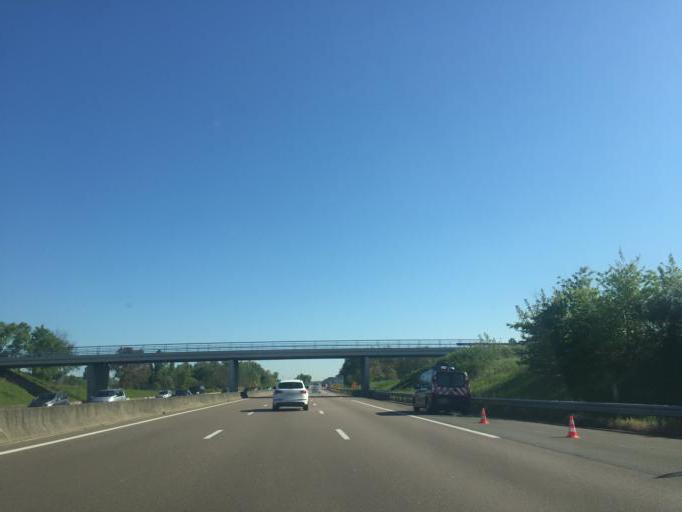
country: FR
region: Bourgogne
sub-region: Departement de Saone-et-Loire
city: Tournus
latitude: 46.4986
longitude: 4.9009
